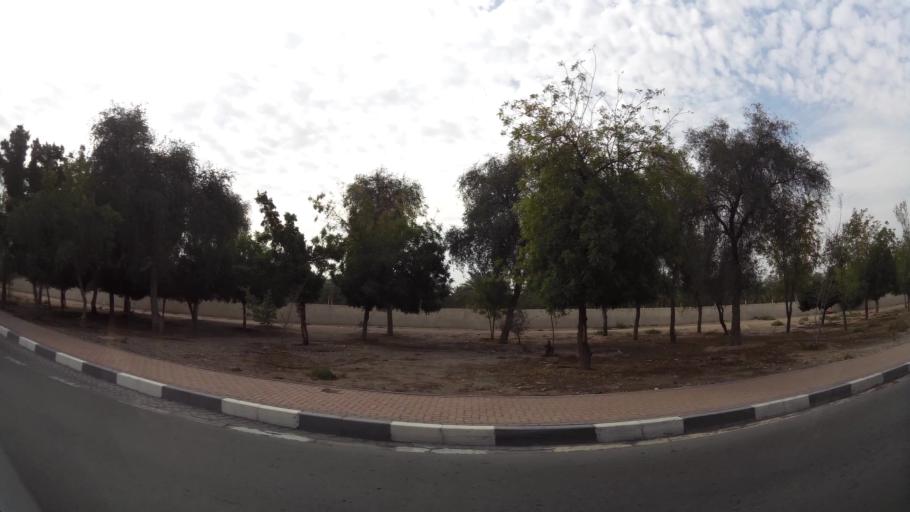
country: AE
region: Abu Dhabi
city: Al Ain
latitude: 24.1767
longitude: 55.6111
